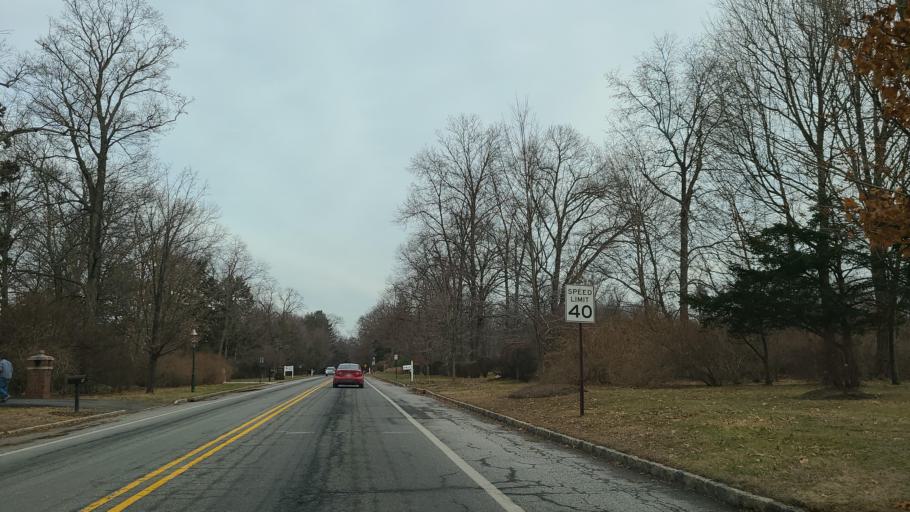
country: US
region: New Jersey
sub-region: Morris County
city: Morristown
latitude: 40.7904
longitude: -74.4541
